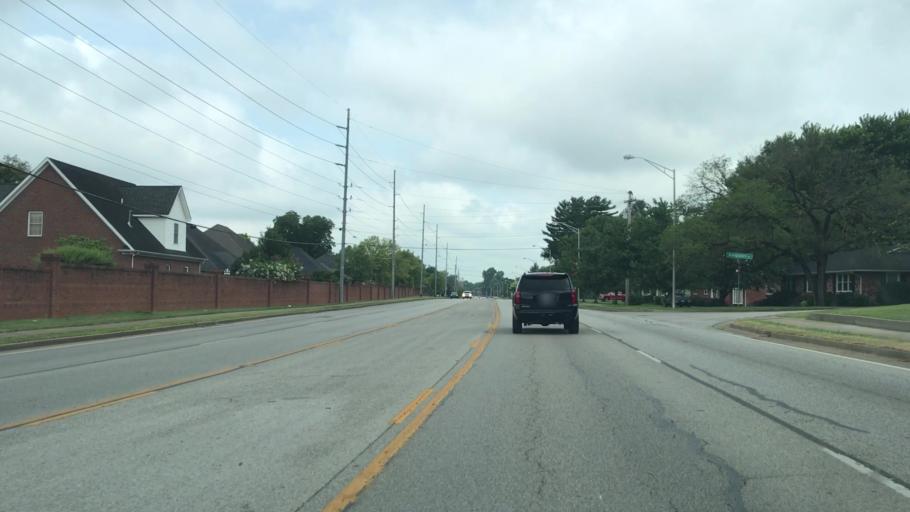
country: US
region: Kentucky
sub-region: Warren County
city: Bowling Green
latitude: 36.9885
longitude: -86.4061
